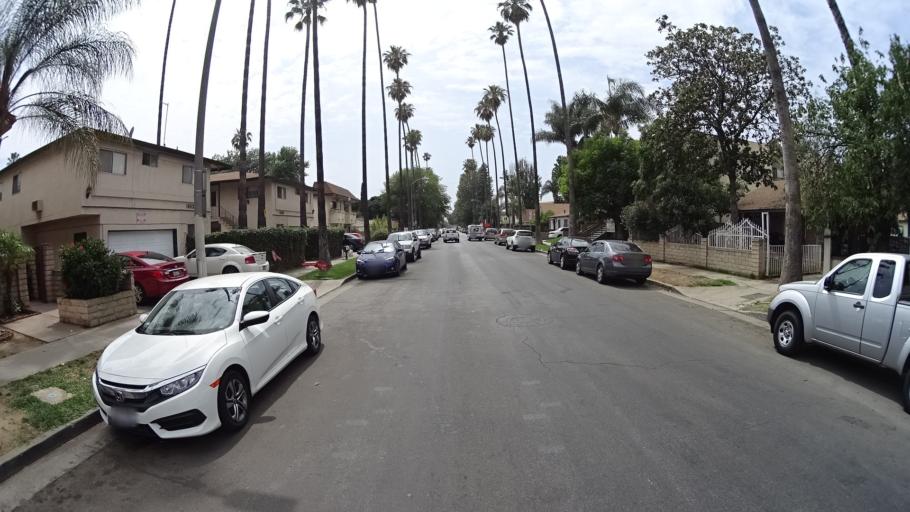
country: US
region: California
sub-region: Los Angeles County
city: Van Nuys
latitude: 34.1836
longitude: -118.4519
